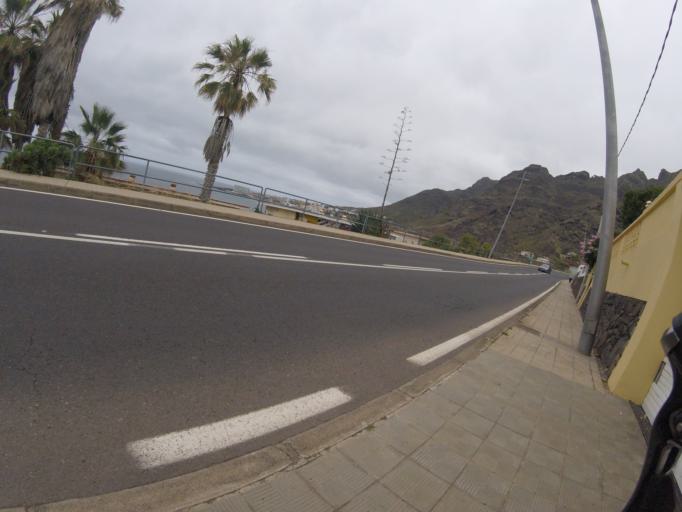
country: ES
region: Canary Islands
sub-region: Provincia de Santa Cruz de Tenerife
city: Tegueste
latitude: 28.5557
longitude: -16.3397
